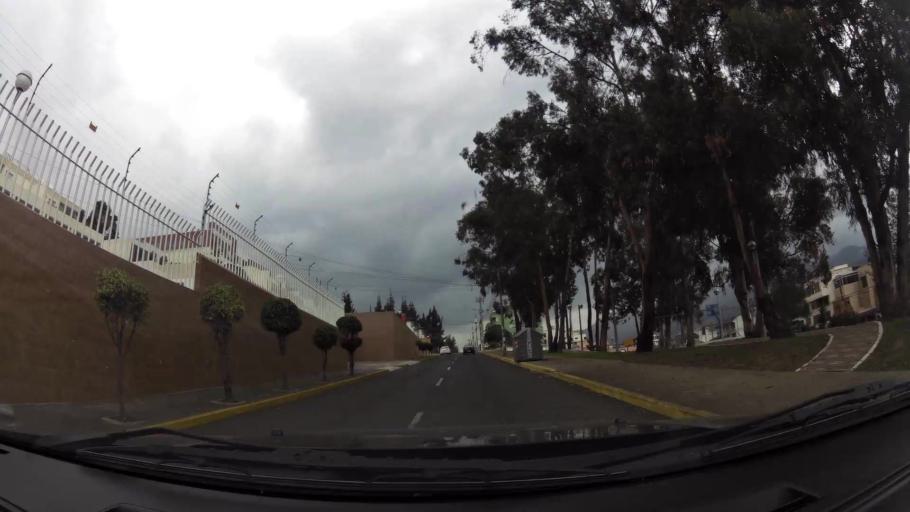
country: EC
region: Pichincha
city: Quito
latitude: -0.0952
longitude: -78.4812
